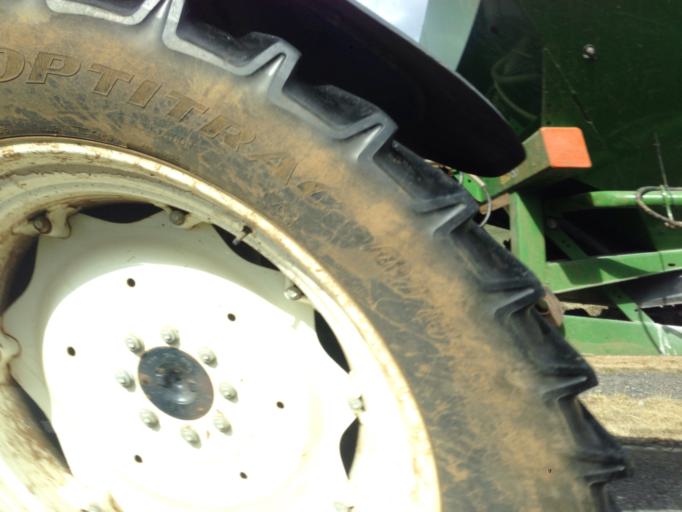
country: IS
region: South
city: Selfoss
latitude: 64.2747
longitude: -20.4061
